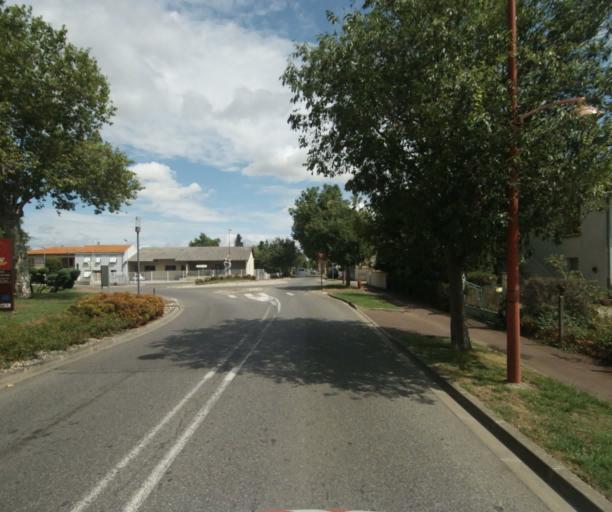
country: FR
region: Midi-Pyrenees
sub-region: Departement de la Haute-Garonne
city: Revel
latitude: 43.4616
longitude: 2.0061
